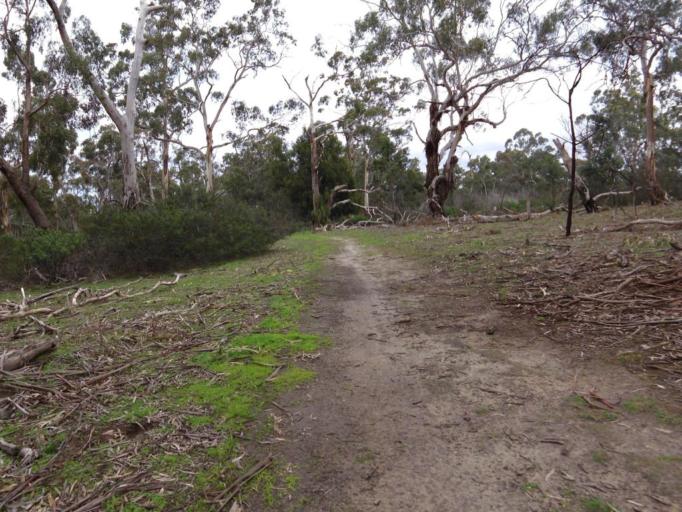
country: AU
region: Victoria
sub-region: Banyule
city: Watsonia North
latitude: -37.6764
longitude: 145.0903
